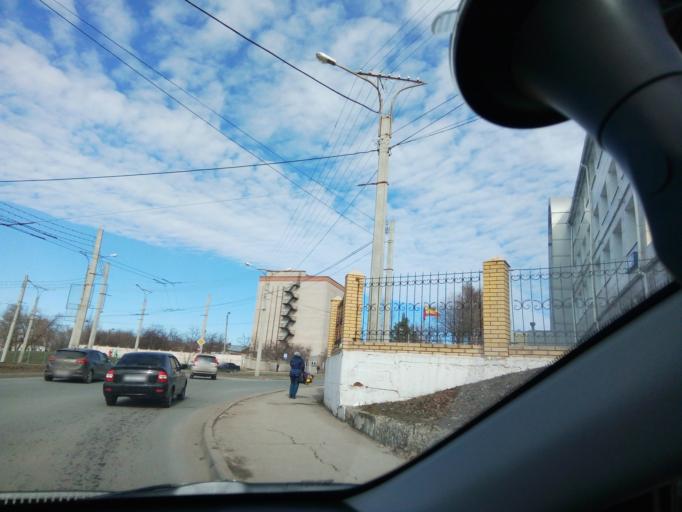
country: RU
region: Chuvashia
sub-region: Cheboksarskiy Rayon
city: Cheboksary
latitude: 56.1114
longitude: 47.2473
